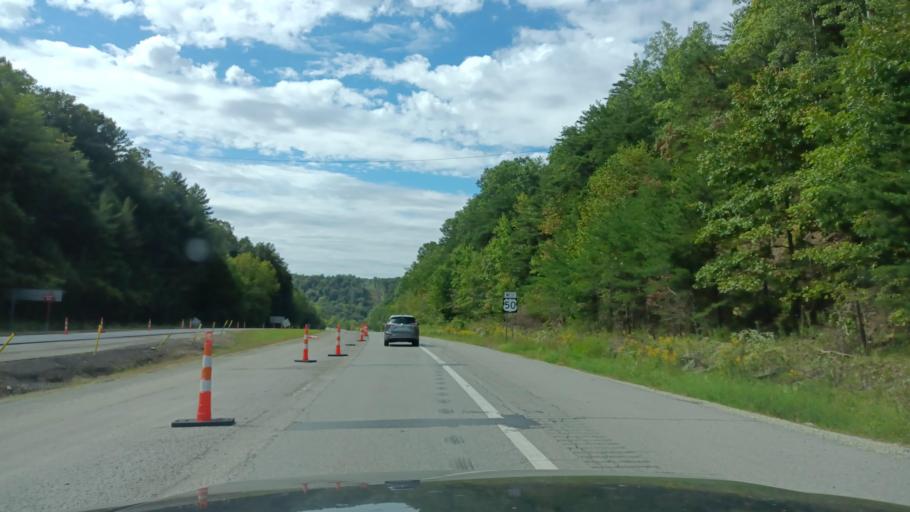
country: US
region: West Virginia
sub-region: Ritchie County
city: Harrisville
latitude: 39.2616
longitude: -81.0925
